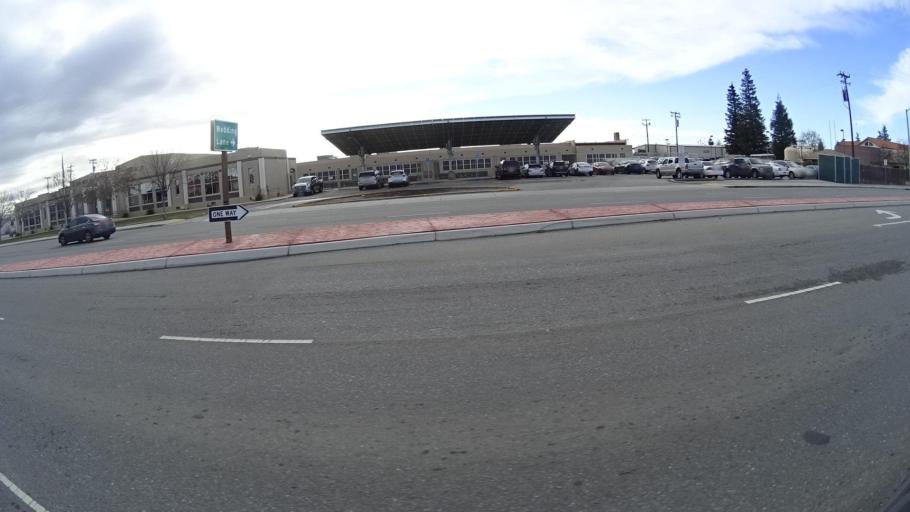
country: US
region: California
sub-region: Kern County
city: Greenacres
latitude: 35.3833
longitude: -119.0820
